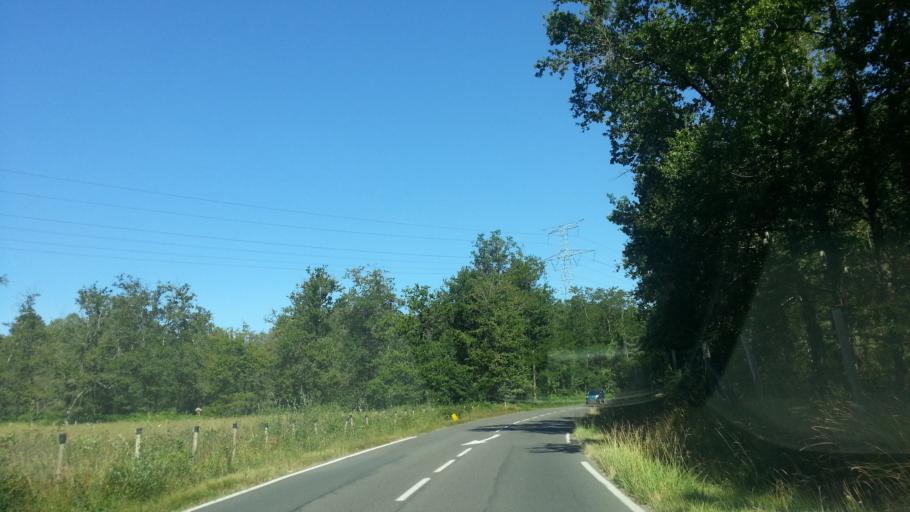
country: FR
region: Aquitaine
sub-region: Departement de la Gironde
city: Saint-Selve
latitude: 44.6762
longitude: -0.4968
